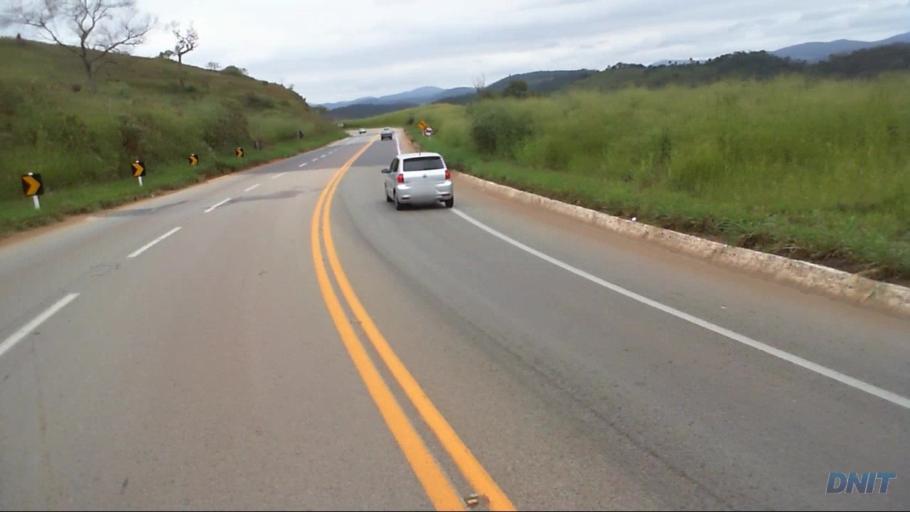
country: BR
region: Minas Gerais
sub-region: Nova Era
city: Nova Era
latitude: -19.7975
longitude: -43.0550
